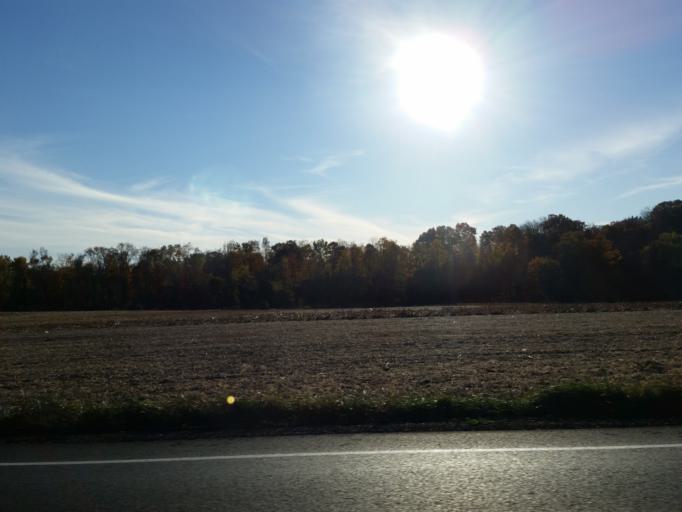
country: US
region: Pennsylvania
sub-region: Lebanon County
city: Annville
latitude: 40.3984
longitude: -76.5728
